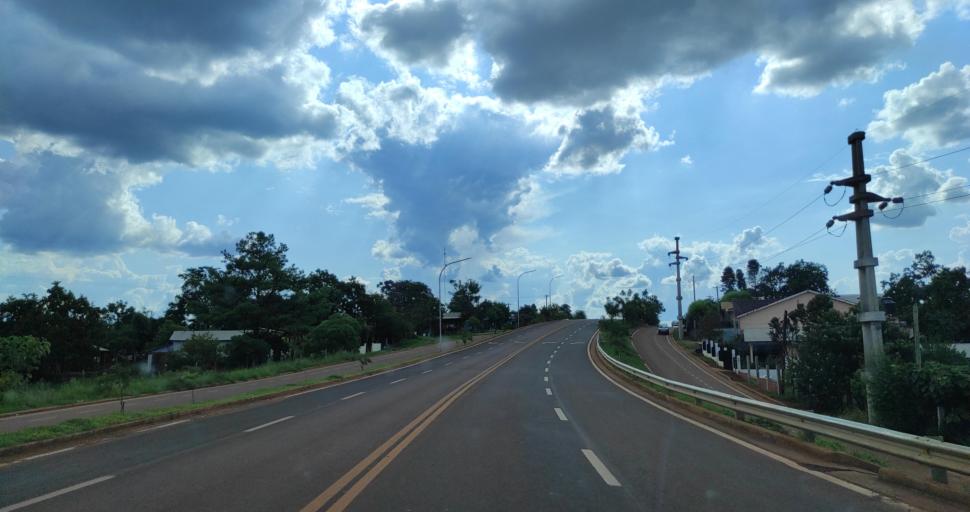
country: AR
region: Misiones
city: Bernardo de Irigoyen
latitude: -26.2955
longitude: -53.7495
